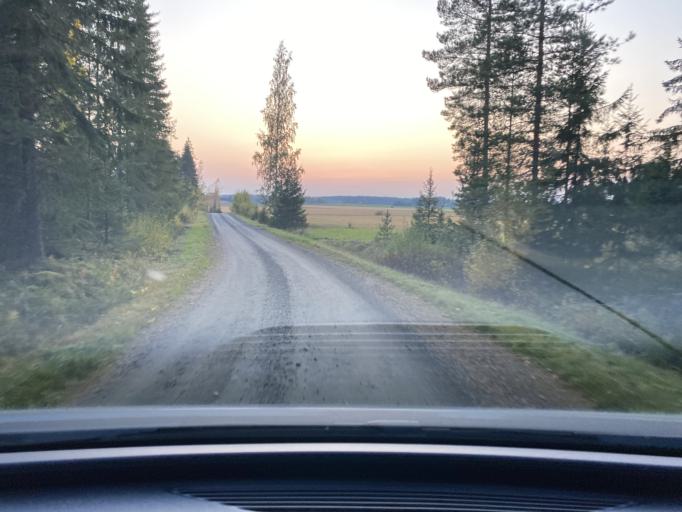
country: FI
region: Pirkanmaa
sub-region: Lounais-Pirkanmaa
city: Punkalaidun
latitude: 61.1101
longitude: 23.2284
